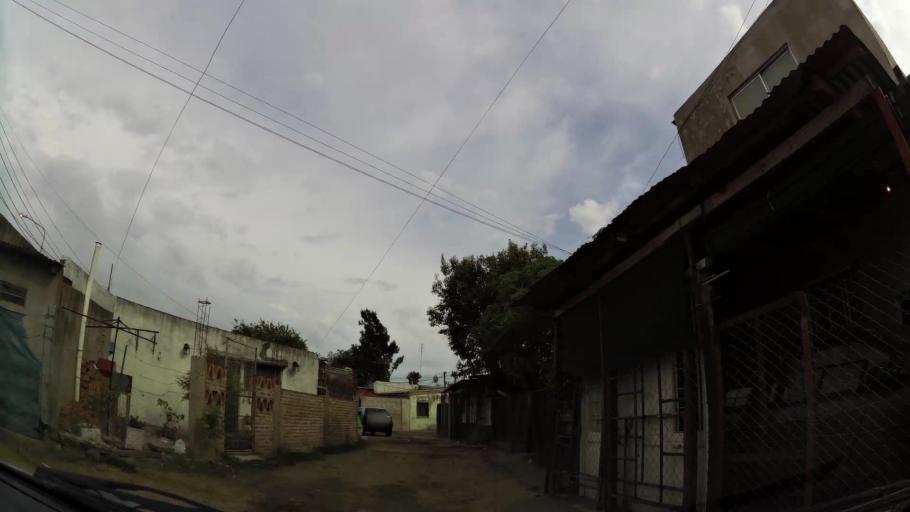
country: AR
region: Buenos Aires
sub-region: Partido de Quilmes
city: Quilmes
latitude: -34.7073
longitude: -58.2654
